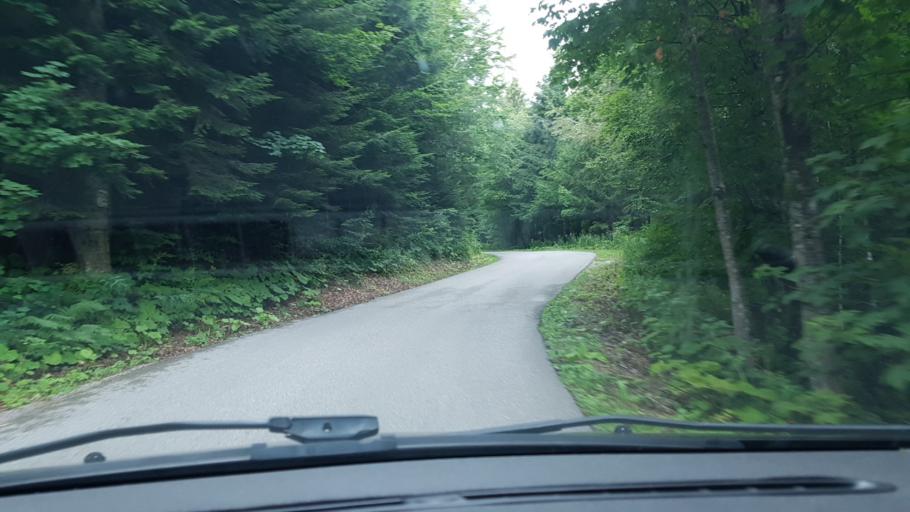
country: HR
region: Primorsko-Goranska
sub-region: Grad Delnice
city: Delnice
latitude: 45.3796
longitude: 14.7003
